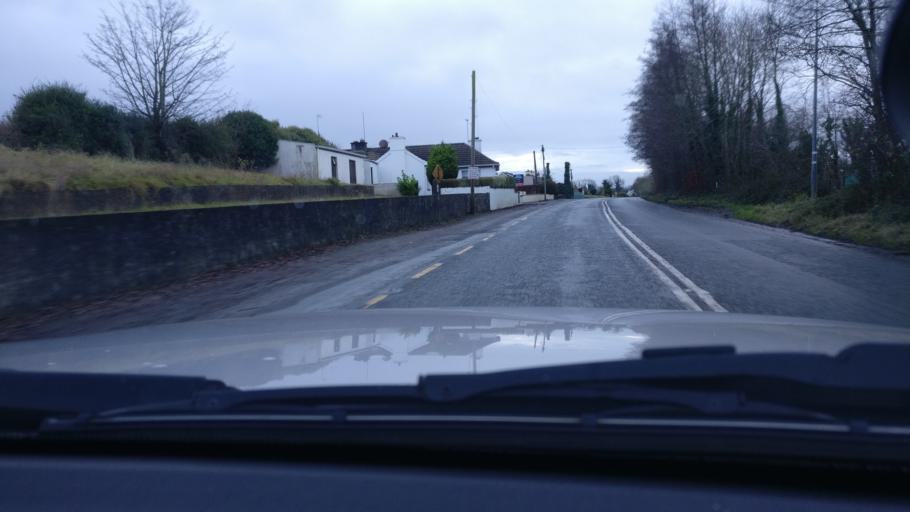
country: IE
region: Leinster
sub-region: An Iarmhi
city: Athlone
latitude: 53.4094
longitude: -7.9845
